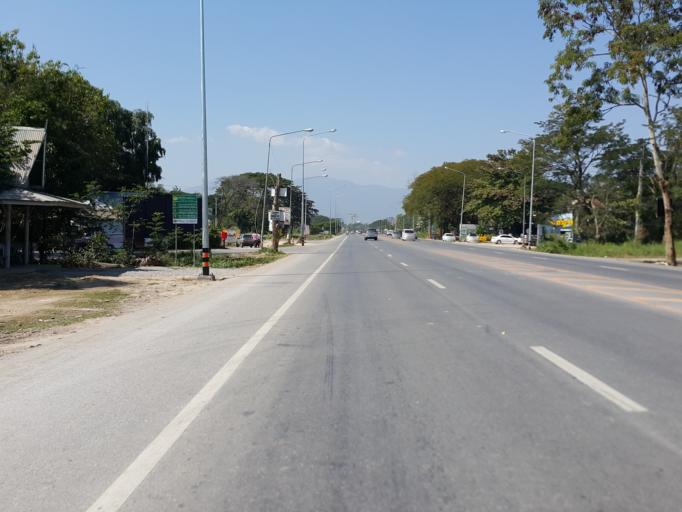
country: TH
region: Chiang Mai
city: Saraphi
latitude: 18.7579
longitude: 99.0484
